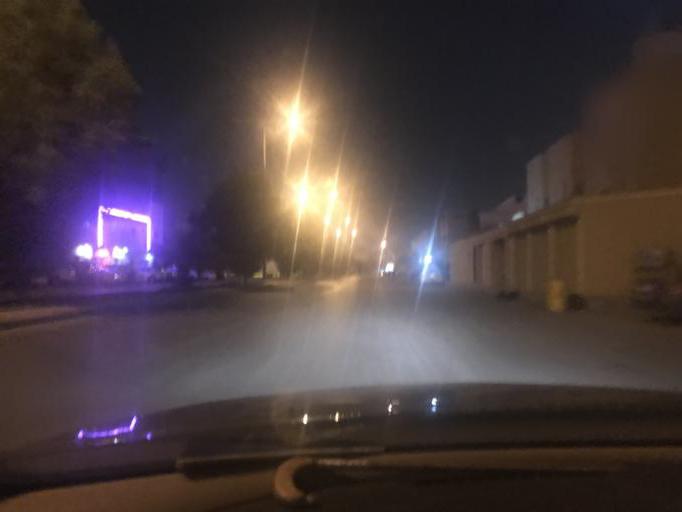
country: SA
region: Ar Riyad
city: Riyadh
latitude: 24.7594
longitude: 46.7613
